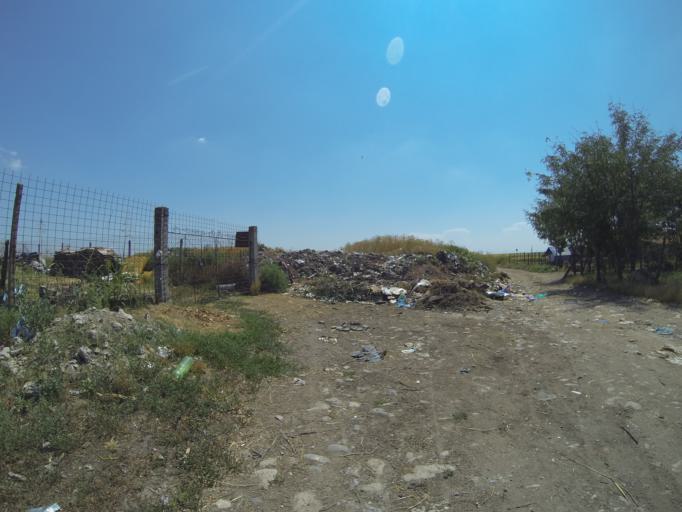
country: RO
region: Dolj
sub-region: Comuna Segarcea
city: Segarcea
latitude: 44.0855
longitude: 23.7399
